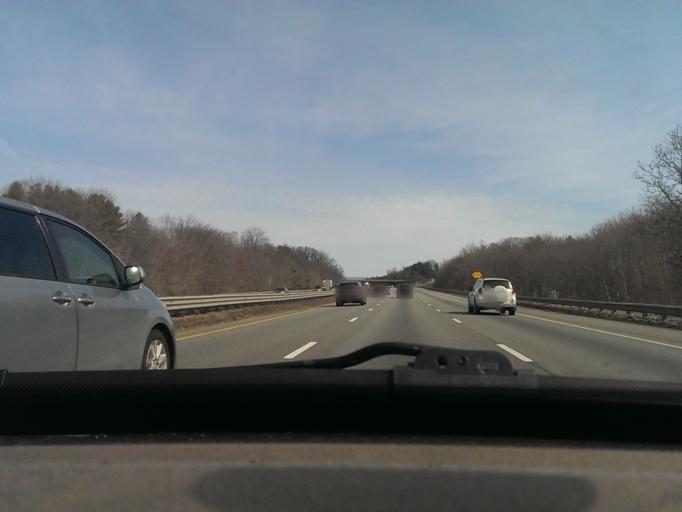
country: US
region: Massachusetts
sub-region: Worcester County
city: Charlton
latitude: 42.1531
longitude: -71.9780
